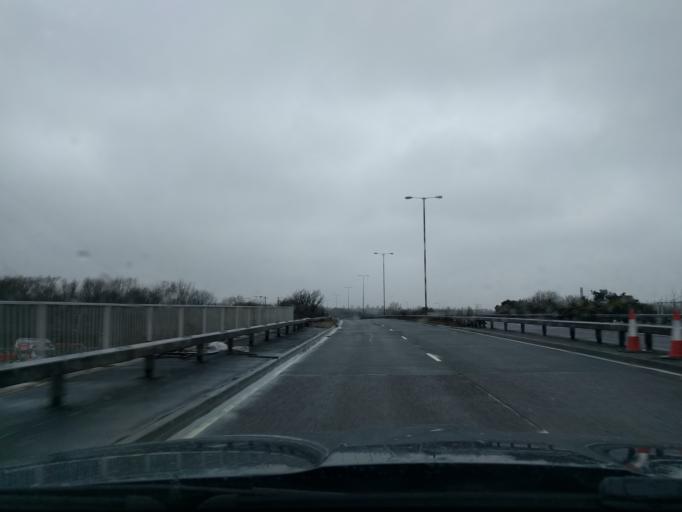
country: GB
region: England
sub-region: South Tyneside
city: Hebburn
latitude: 54.9457
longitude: -1.5147
